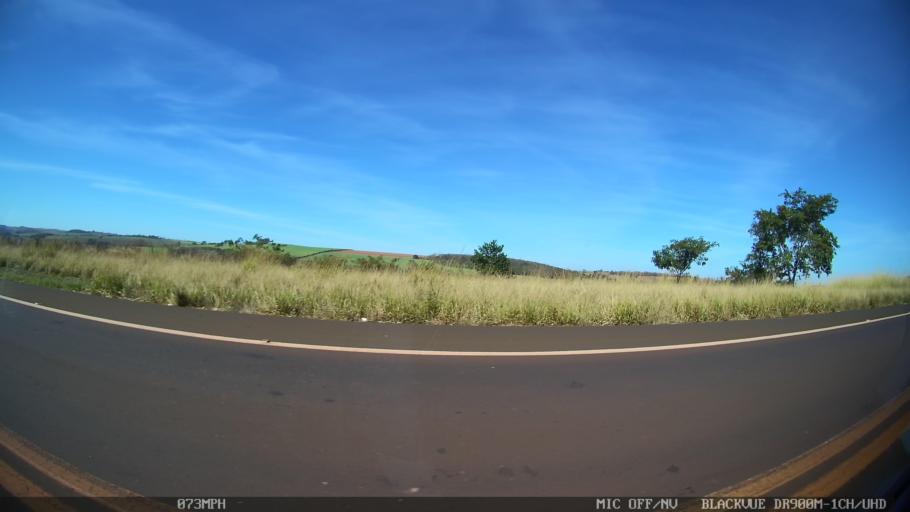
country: BR
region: Sao Paulo
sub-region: Sao Joaquim Da Barra
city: Sao Joaquim da Barra
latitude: -20.5604
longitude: -47.6842
